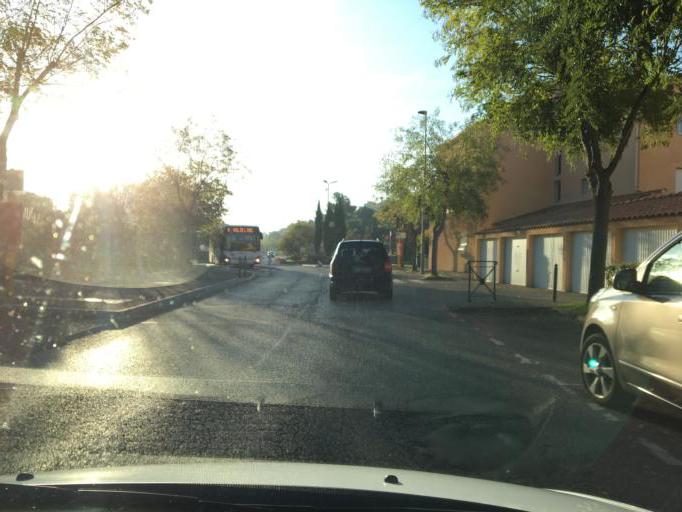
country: FR
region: Provence-Alpes-Cote d'Azur
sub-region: Departement des Bouches-du-Rhone
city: Aix-en-Provence
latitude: 43.5285
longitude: 5.4106
